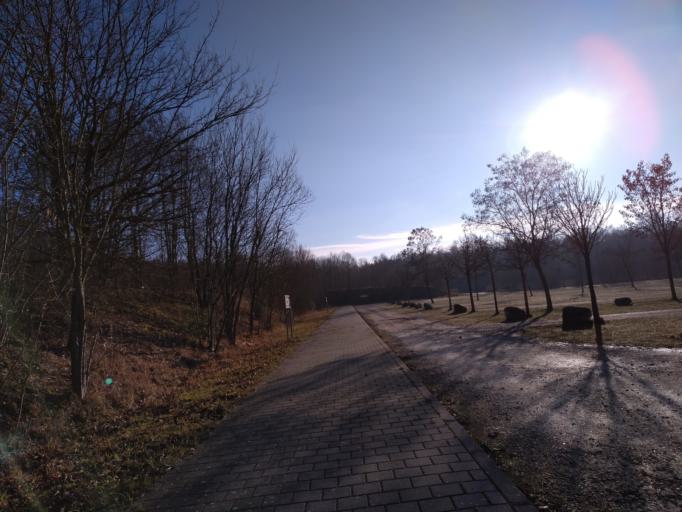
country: DE
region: Bavaria
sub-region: Swabia
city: Wasserburg
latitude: 48.4222
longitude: 10.3001
